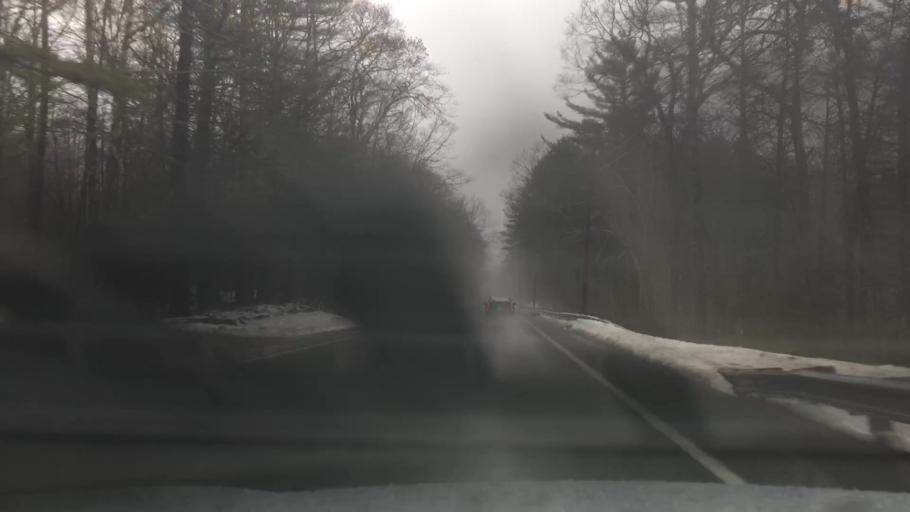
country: US
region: Massachusetts
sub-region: Franklin County
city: Orange
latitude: 42.5236
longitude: -72.3233
